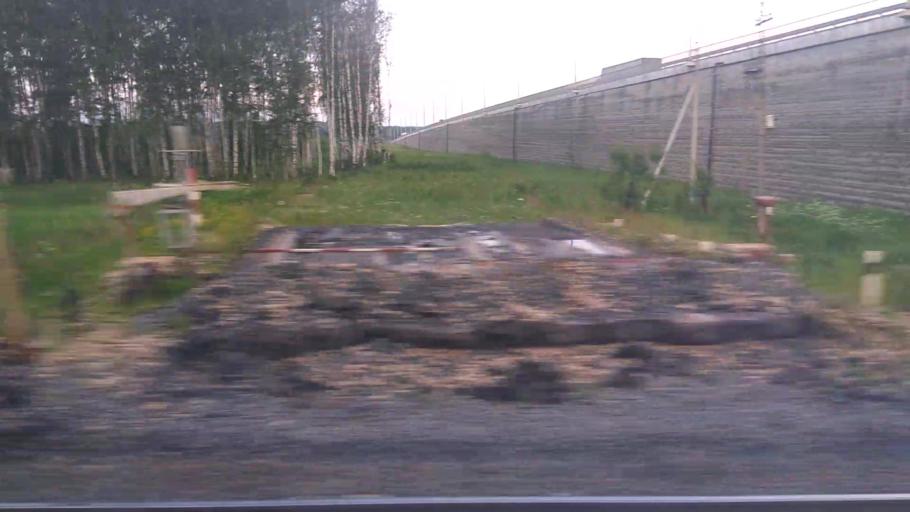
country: RU
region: Moskovskaya
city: Mikhnevo
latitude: 55.0843
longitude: 37.9730
